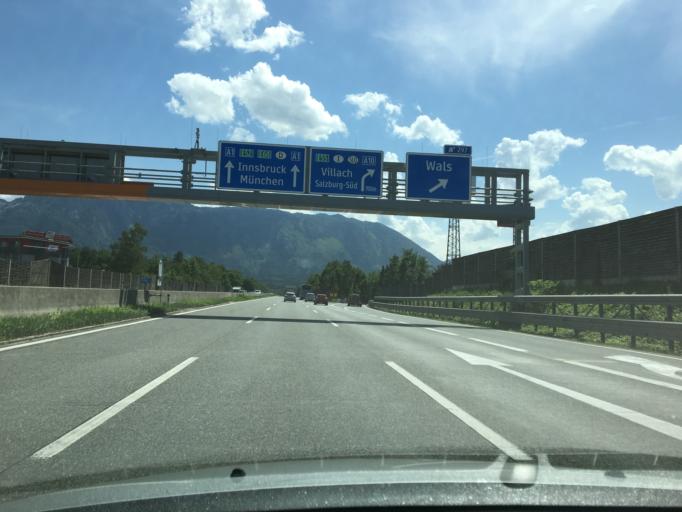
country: DE
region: Bavaria
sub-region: Upper Bavaria
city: Ainring
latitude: 47.7892
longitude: 12.9819
